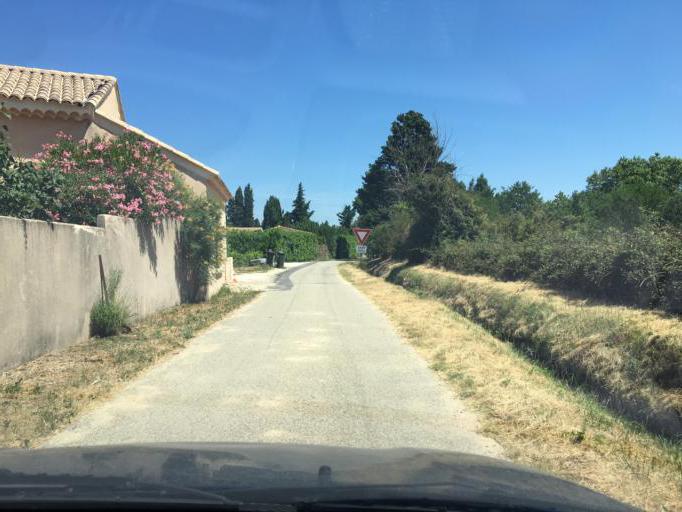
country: FR
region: Provence-Alpes-Cote d'Azur
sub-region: Departement du Vaucluse
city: Camaret-sur-Aigues
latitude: 44.1625
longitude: 4.8914
